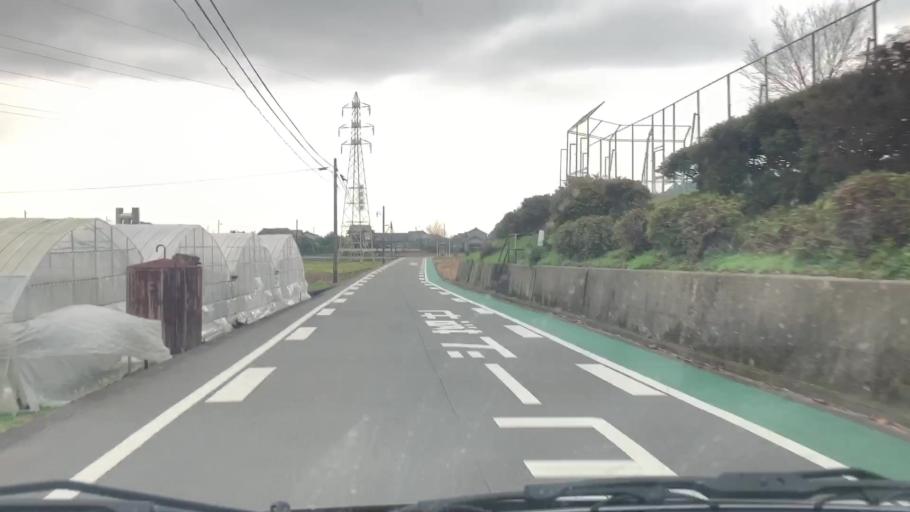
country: JP
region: Saga Prefecture
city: Kashima
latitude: 33.1225
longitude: 130.0580
